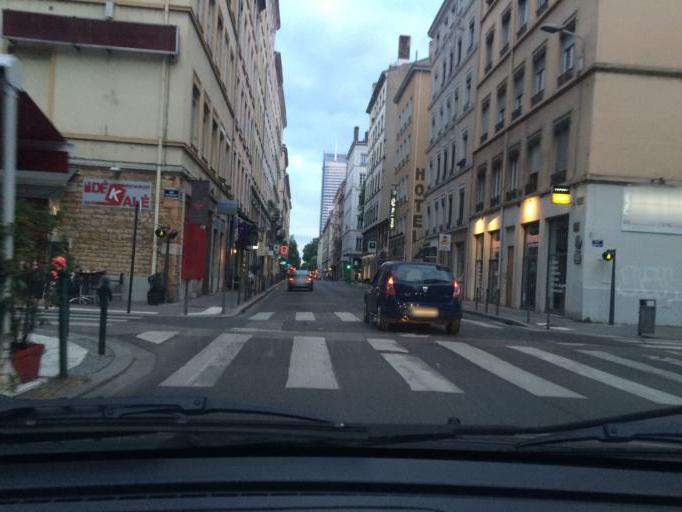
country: FR
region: Rhone-Alpes
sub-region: Departement du Rhone
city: Caluire-et-Cuire
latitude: 45.7704
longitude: 4.8504
